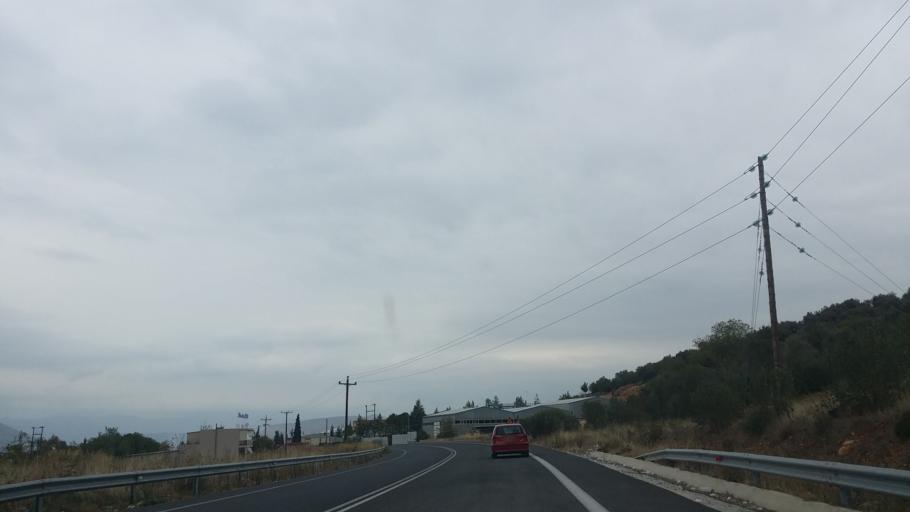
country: GR
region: Central Greece
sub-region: Nomos Voiotias
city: Thivai
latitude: 38.3203
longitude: 23.2704
